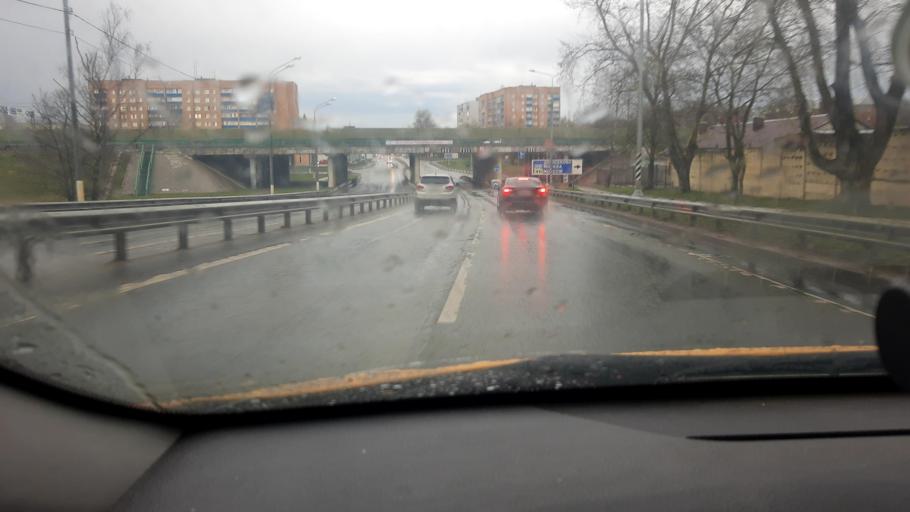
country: RU
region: Moskovskaya
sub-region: Volokolamskiy Rayon
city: Volokolamsk
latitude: 56.0246
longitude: 35.9462
